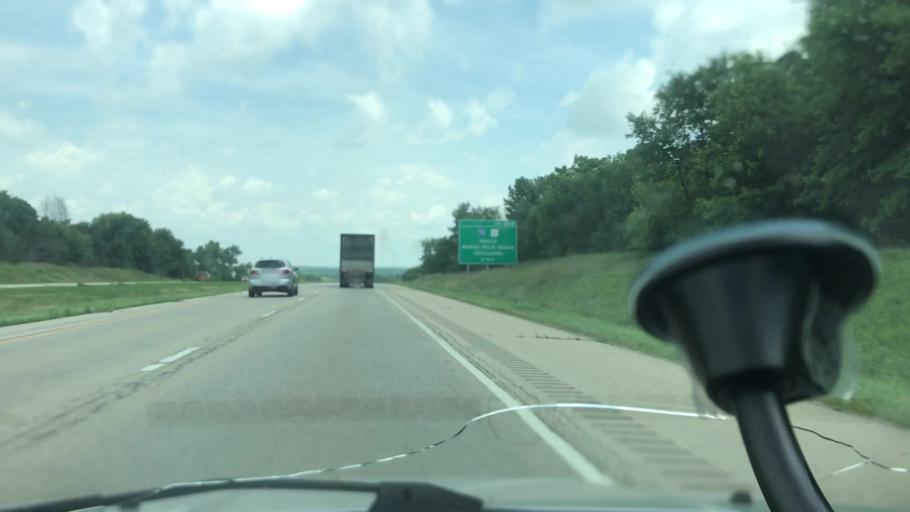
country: US
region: Illinois
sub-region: Peoria County
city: Bellevue
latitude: 40.7043
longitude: -89.6758
